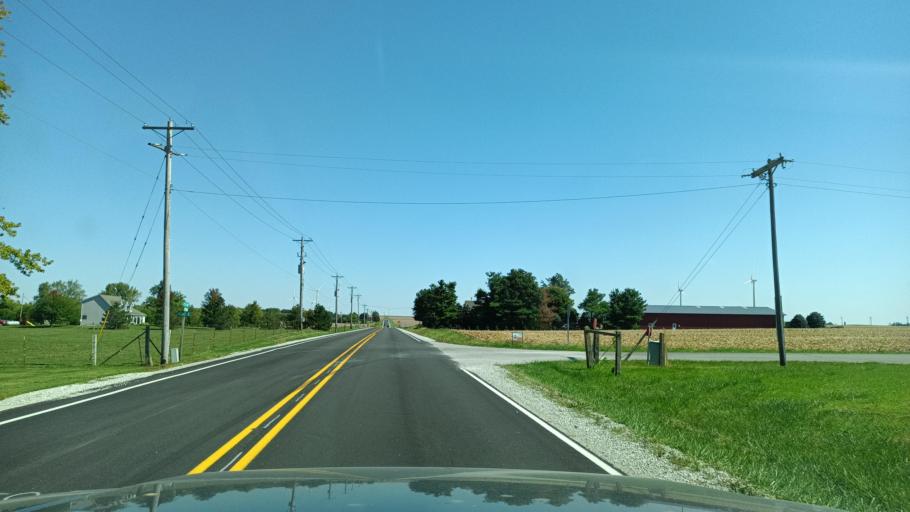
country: US
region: Illinois
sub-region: McLean County
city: Danvers
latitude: 40.5826
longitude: -89.1195
